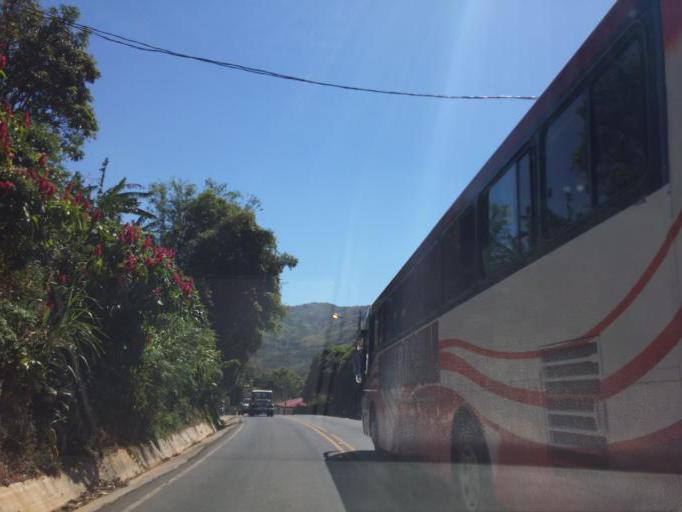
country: CR
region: Heredia
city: Colon
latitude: 9.8995
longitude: -84.2352
